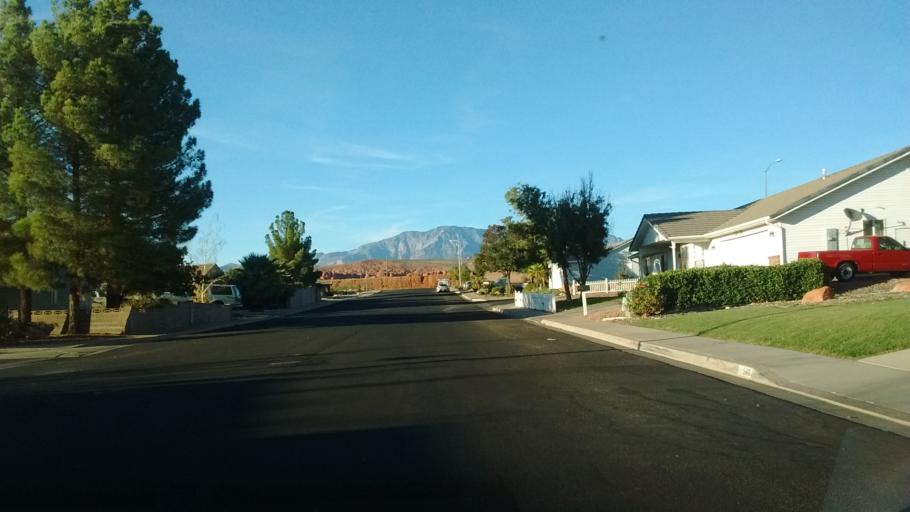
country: US
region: Utah
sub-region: Washington County
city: Washington
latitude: 37.1394
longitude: -113.4977
